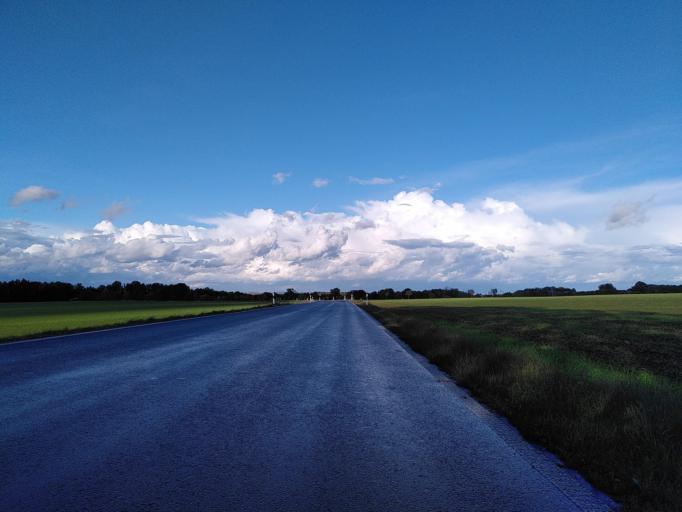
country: DE
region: Saxony
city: Heidenau
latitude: 51.0310
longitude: 13.9027
